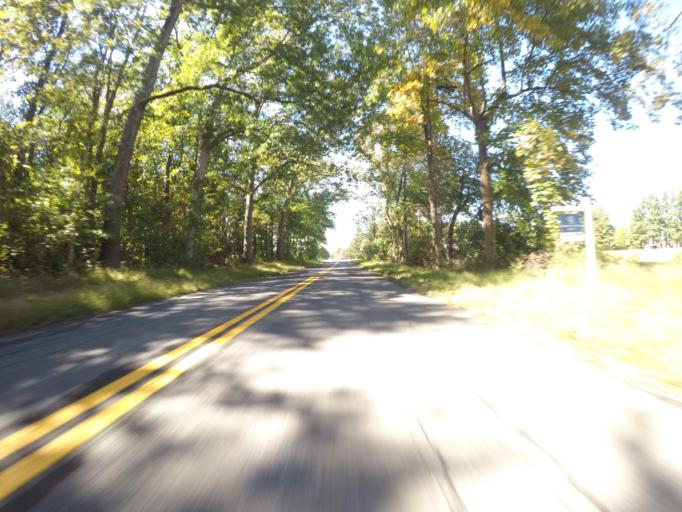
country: US
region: Maryland
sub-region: Carroll County
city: Hampstead
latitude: 39.5550
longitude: -76.8290
